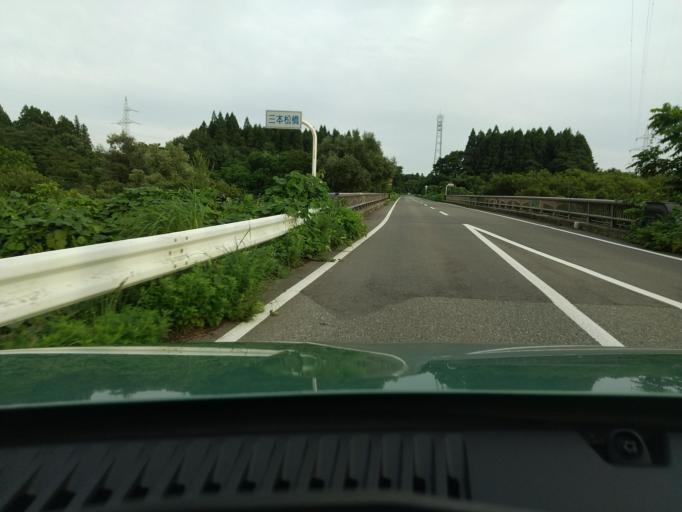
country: JP
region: Akita
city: Akita
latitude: 39.7613
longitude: 140.1589
